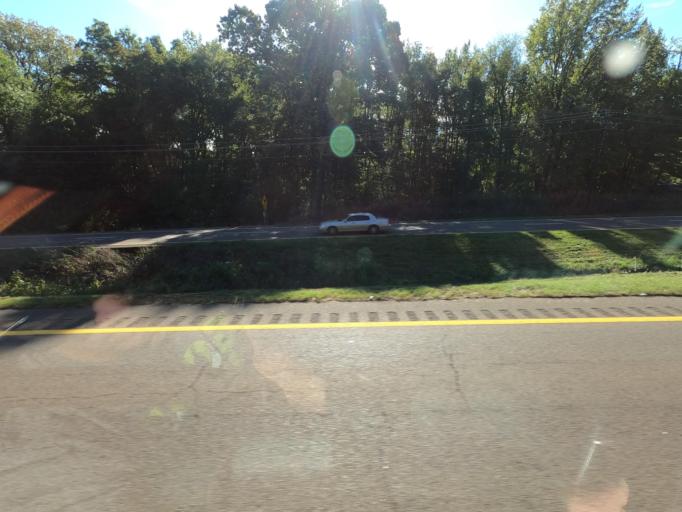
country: US
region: Tennessee
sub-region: Tipton County
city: Atoka
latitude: 35.4678
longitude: -89.7560
